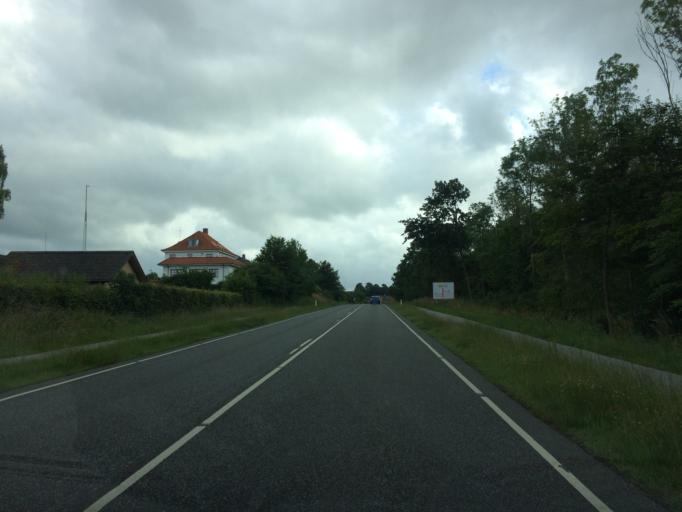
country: DK
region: South Denmark
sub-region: Sonderborg Kommune
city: Guderup
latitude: 54.9897
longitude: 9.9787
